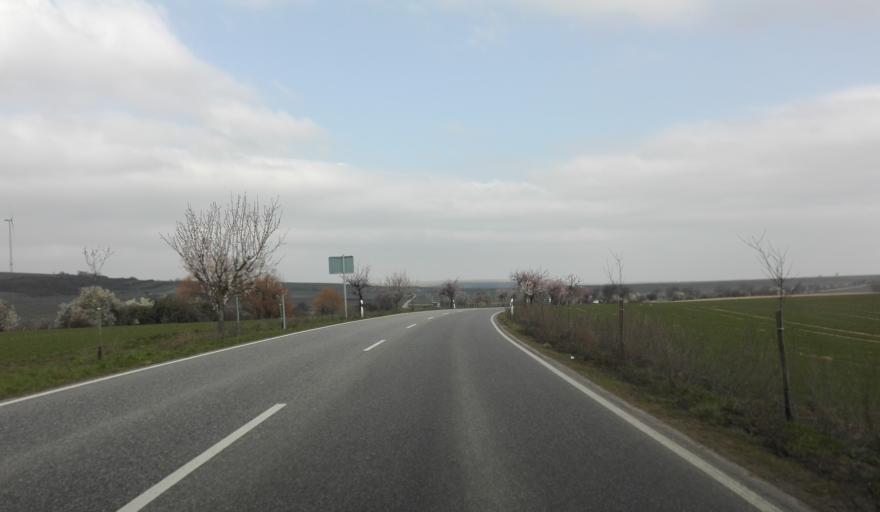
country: DE
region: Rheinland-Pfalz
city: Bockenheim
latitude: 49.6142
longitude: 8.1815
